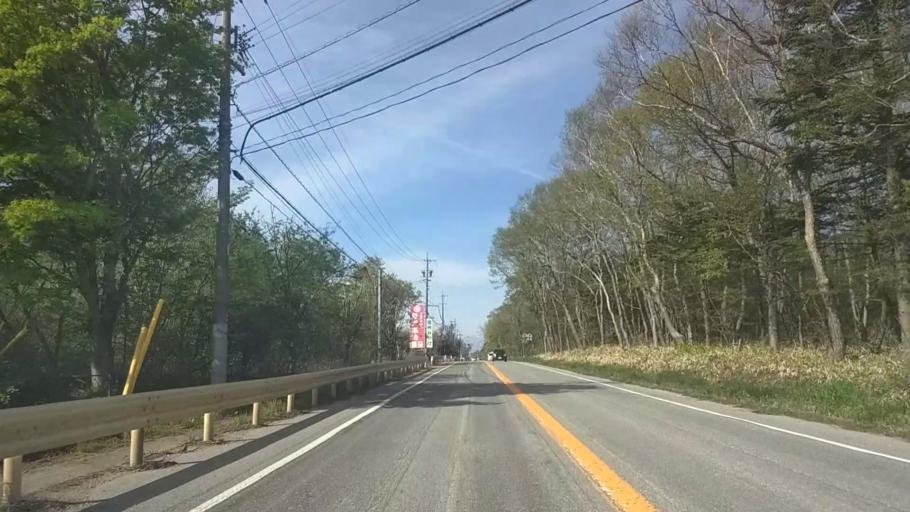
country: JP
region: Yamanashi
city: Nirasaki
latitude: 35.9552
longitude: 138.4627
